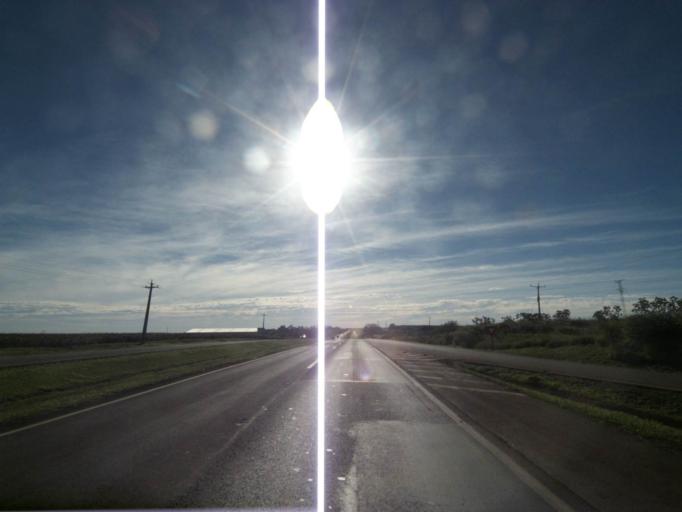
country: BR
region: Parana
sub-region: Cascavel
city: Cascavel
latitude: -25.0222
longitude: -53.5482
